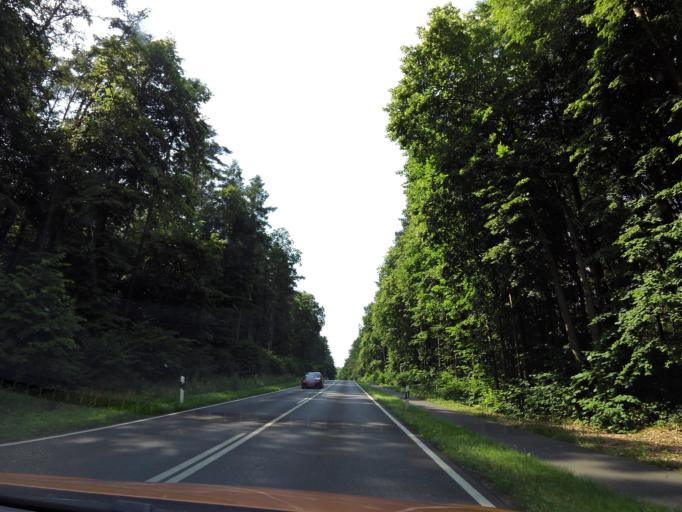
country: DE
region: Mecklenburg-Vorpommern
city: Muhl Rosin
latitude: 53.7842
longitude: 12.2321
